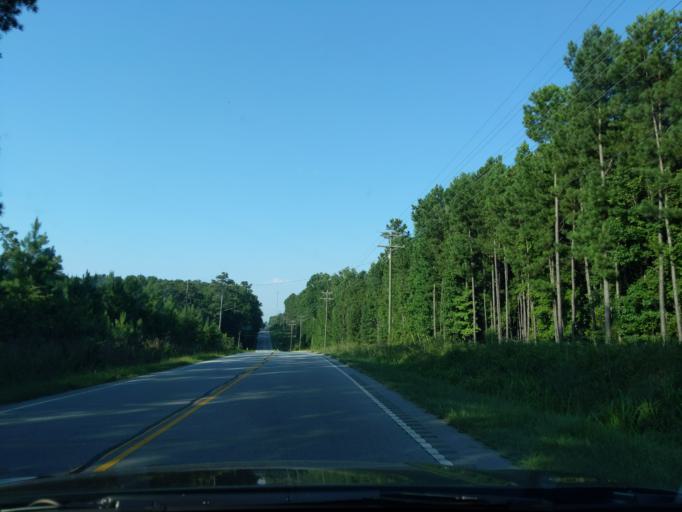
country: US
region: South Carolina
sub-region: Newberry County
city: Newberry
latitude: 34.3027
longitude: -81.5881
